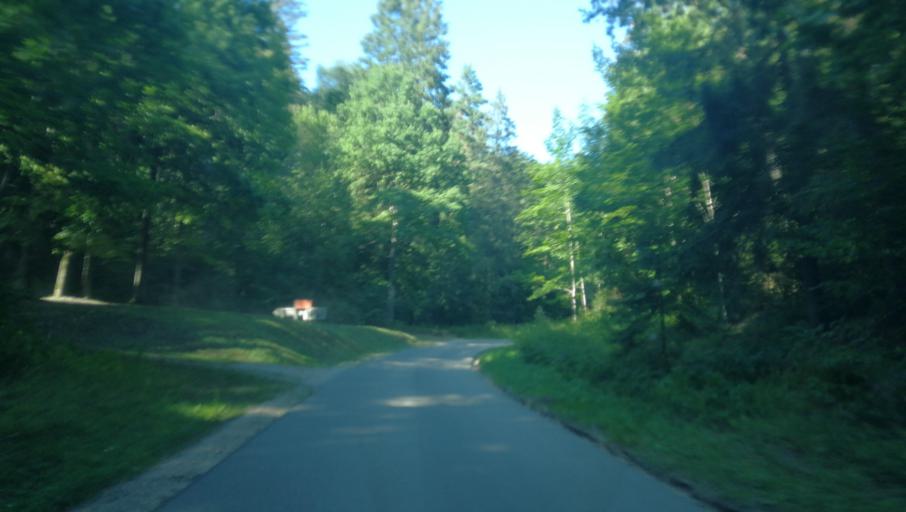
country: LV
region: Cesu Rajons
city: Cesis
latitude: 57.2854
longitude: 25.2148
